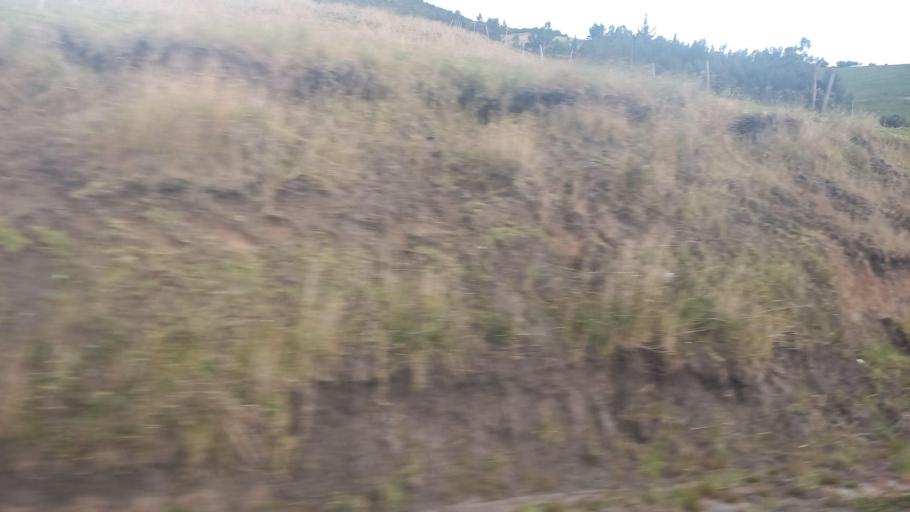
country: EC
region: Pichincha
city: Cayambe
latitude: 0.1034
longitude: -78.0817
